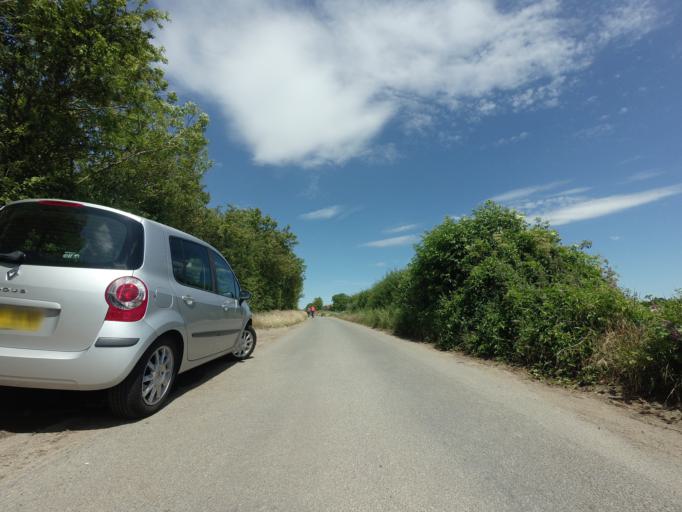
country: GB
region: England
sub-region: Kent
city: Cliffe
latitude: 51.4557
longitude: 0.4907
